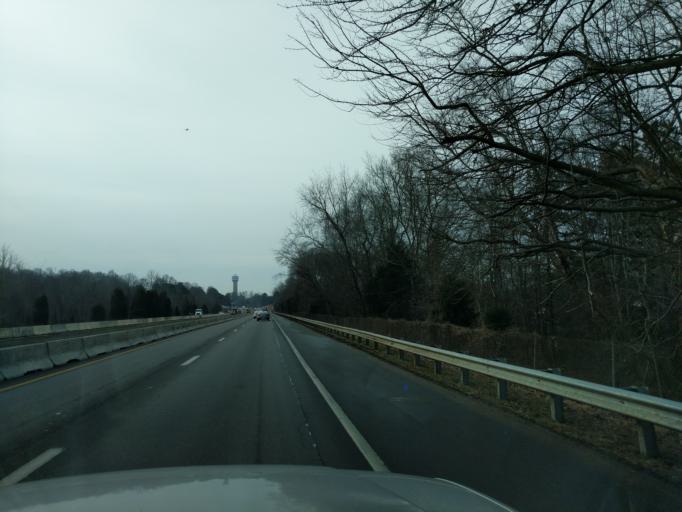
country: US
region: North Carolina
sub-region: Iredell County
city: Mooresville
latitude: 35.5698
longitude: -80.8572
